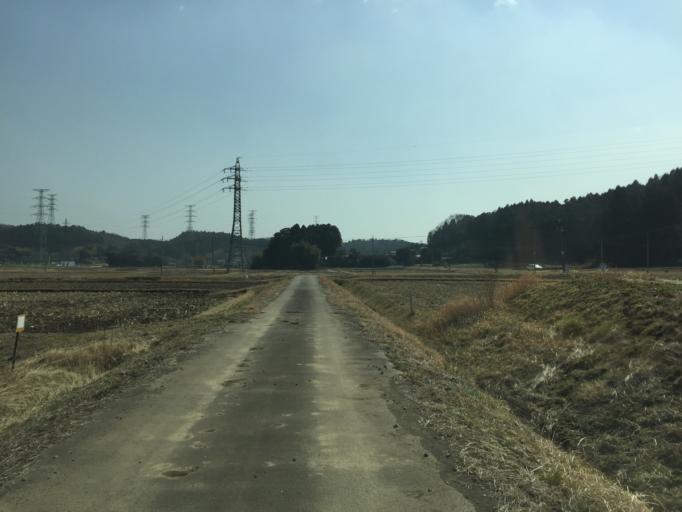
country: JP
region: Fukushima
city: Iwaki
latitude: 36.9393
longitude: 140.7919
